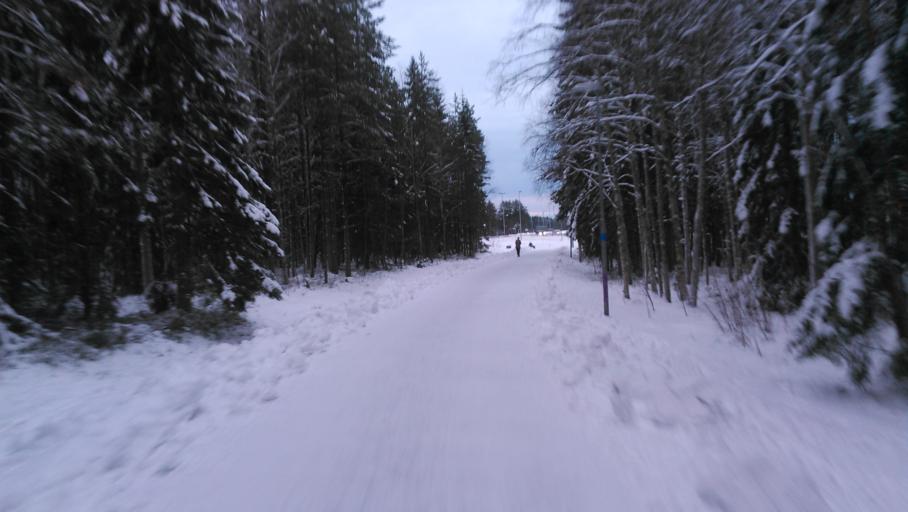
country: SE
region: Vaesterbotten
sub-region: Umea Kommun
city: Ersmark
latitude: 63.8155
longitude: 20.3278
